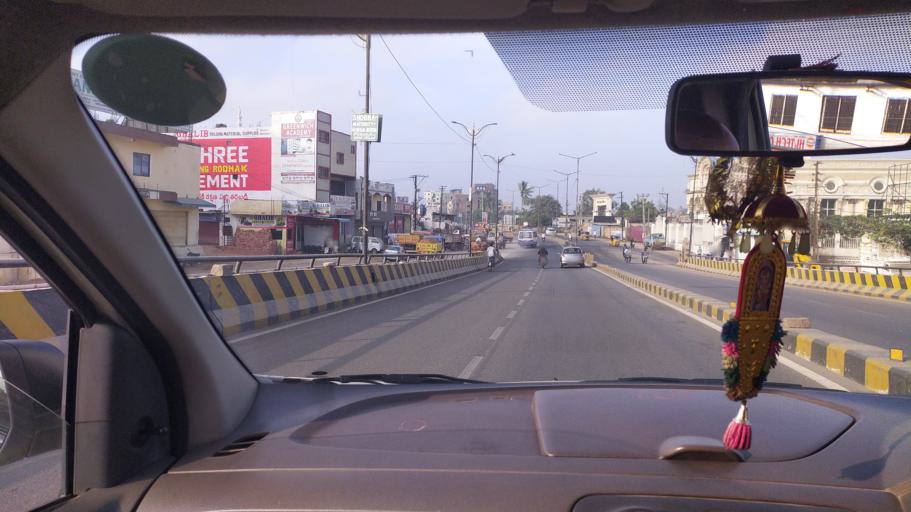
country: IN
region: Telangana
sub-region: Rangareddi
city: Balapur
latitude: 17.3262
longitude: 78.4749
